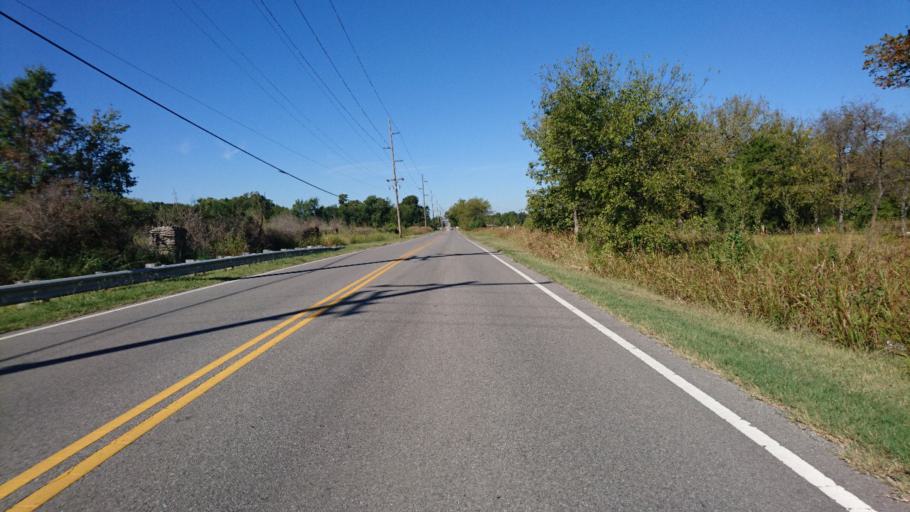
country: US
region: Oklahoma
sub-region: Rogers County
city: Catoosa
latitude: 36.1480
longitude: -95.8070
